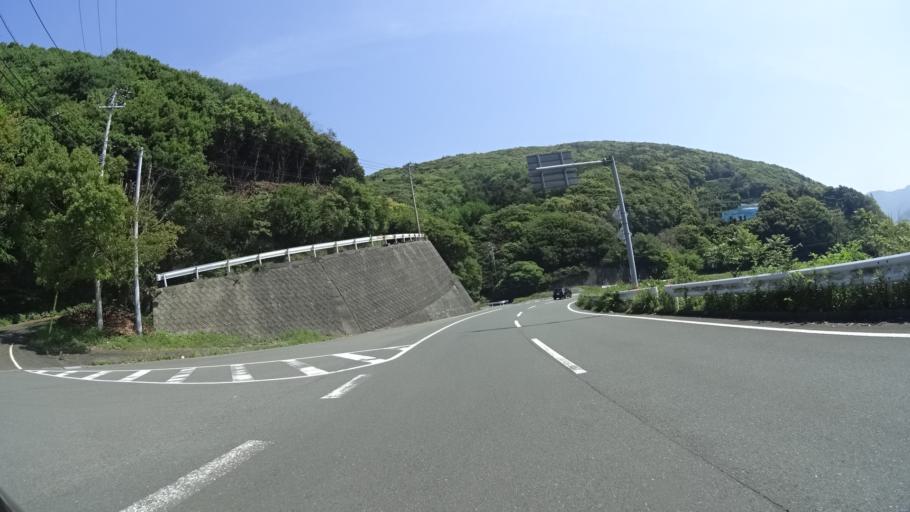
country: JP
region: Ehime
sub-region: Nishiuwa-gun
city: Ikata-cho
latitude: 33.3891
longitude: 132.0931
